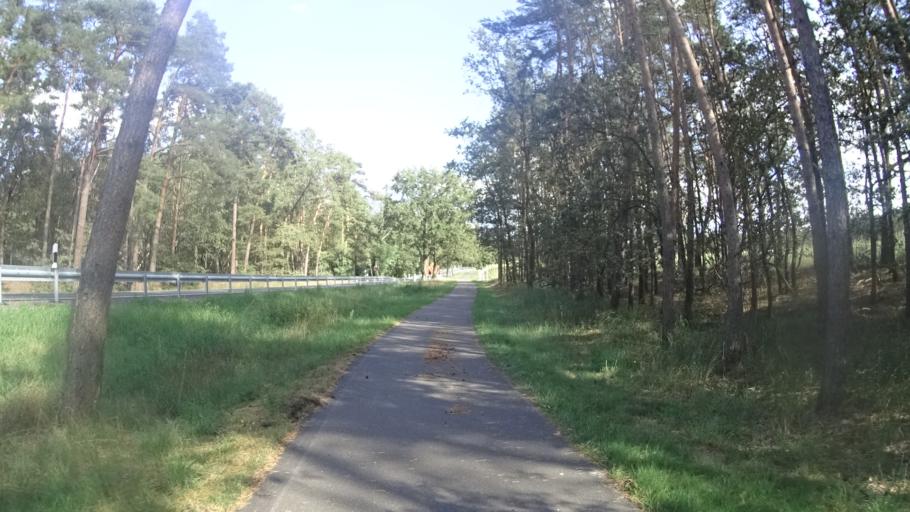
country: DE
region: Brandenburg
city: Rhinow
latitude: 52.7301
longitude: 12.3493
